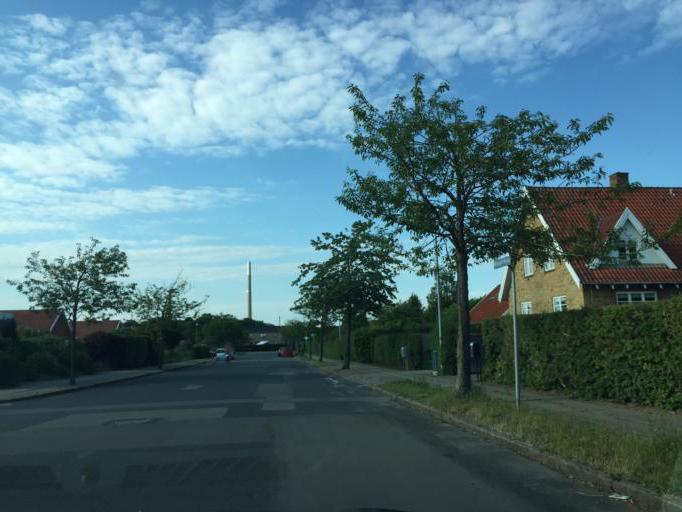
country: DK
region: South Denmark
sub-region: Odense Kommune
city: Stige
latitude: 55.4160
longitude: 10.4059
